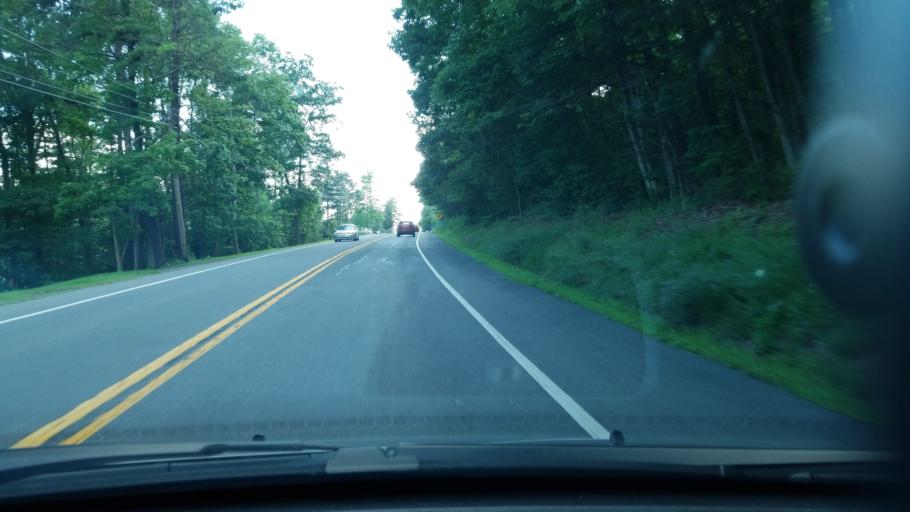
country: US
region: Pennsylvania
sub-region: Northumberland County
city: Elysburg
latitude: 40.8775
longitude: -76.5097
